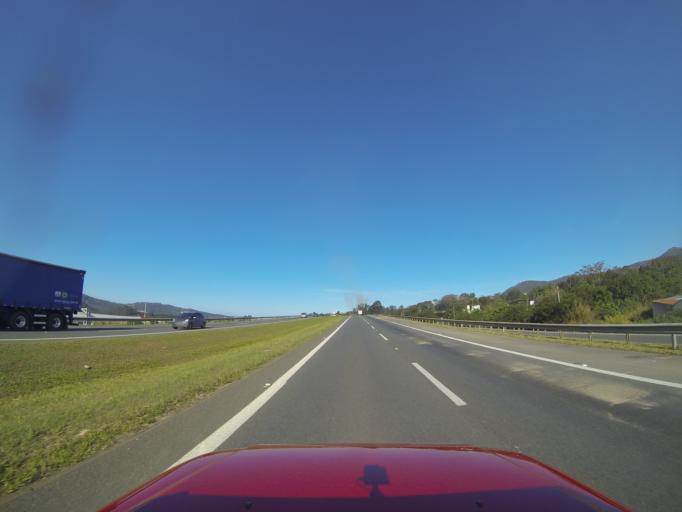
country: BR
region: Sao Paulo
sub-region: Atibaia
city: Atibaia
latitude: -23.1089
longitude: -46.5224
